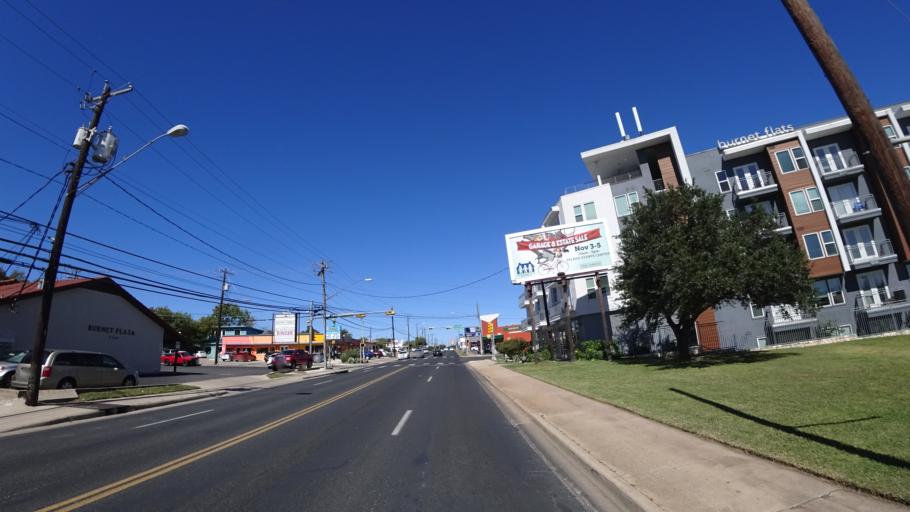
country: US
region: Texas
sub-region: Travis County
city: Austin
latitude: 30.3297
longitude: -97.7399
